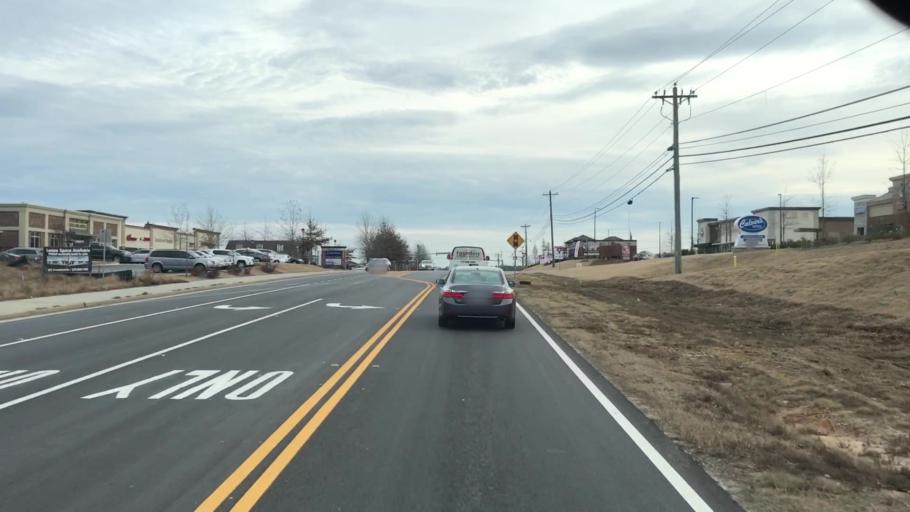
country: US
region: Georgia
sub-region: Jackson County
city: Braselton
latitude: 34.1216
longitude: -83.8272
